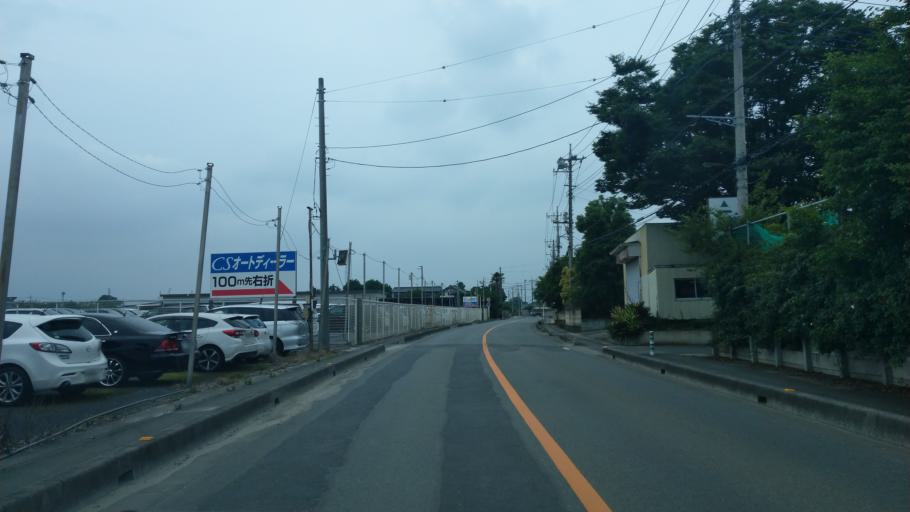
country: JP
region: Saitama
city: Iwatsuki
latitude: 35.9305
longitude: 139.6910
